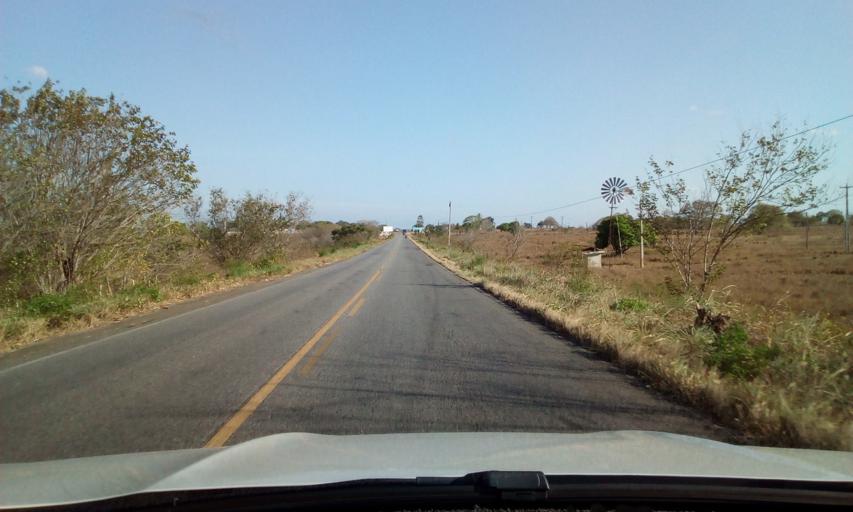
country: BR
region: Paraiba
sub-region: Guarabira
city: Guarabira
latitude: -6.9240
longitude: -35.4441
